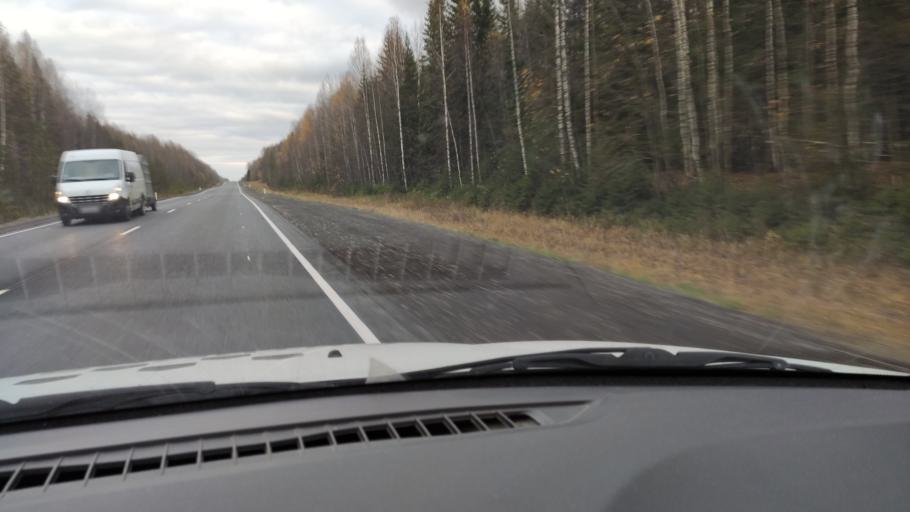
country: RU
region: Kirov
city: Chernaya Kholunitsa
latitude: 58.8829
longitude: 51.4182
